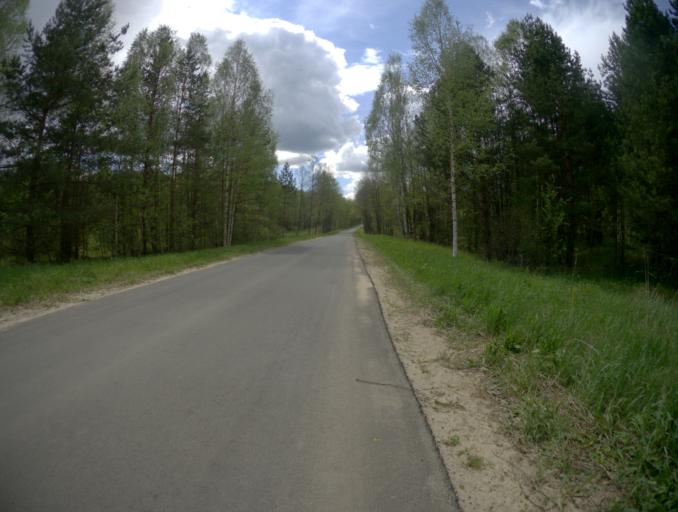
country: RU
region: Vladimir
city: Velikodvorskiy
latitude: 55.2533
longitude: 40.7730
